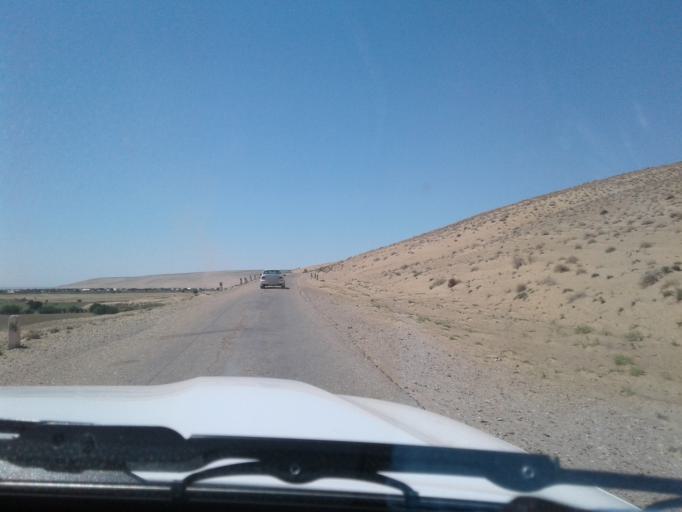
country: AF
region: Badghis
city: Bala Murghab
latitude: 35.9753
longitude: 62.9017
